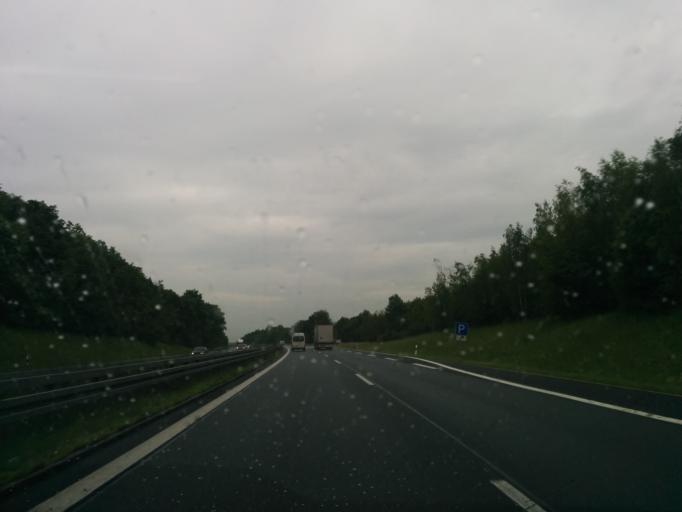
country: DE
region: Bavaria
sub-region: Regierungsbezirk Unterfranken
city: Kurnach
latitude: 49.8285
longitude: 10.0413
